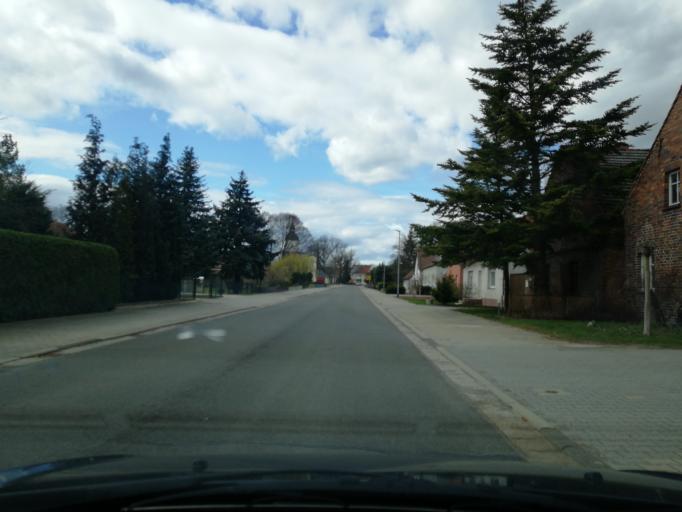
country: DE
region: Brandenburg
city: Altdobern
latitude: 51.7130
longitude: 14.0440
